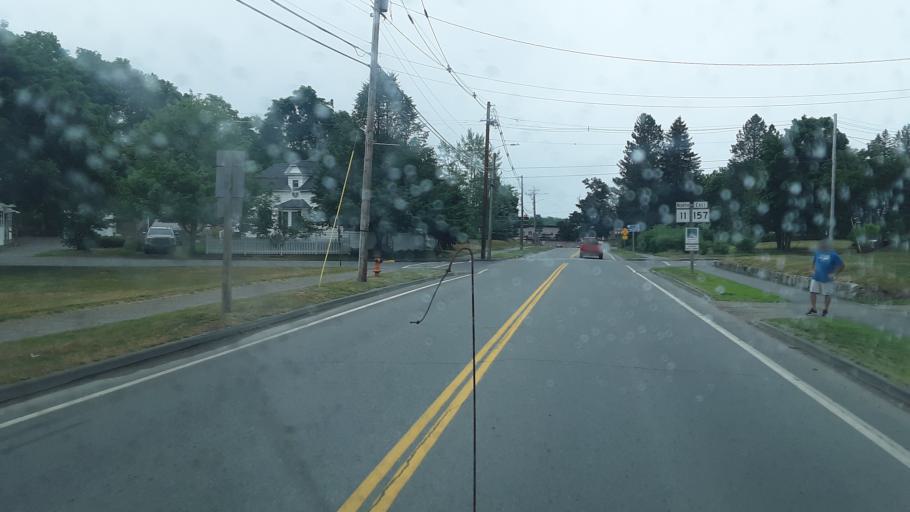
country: US
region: Maine
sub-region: Penobscot County
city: Millinocket
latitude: 45.6580
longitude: -68.7120
